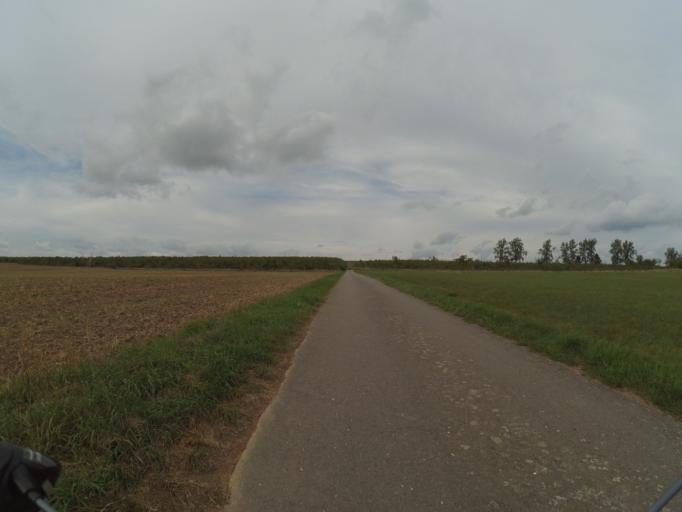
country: DE
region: Rheinland-Pfalz
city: Herforst
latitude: 49.9614
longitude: 6.6907
